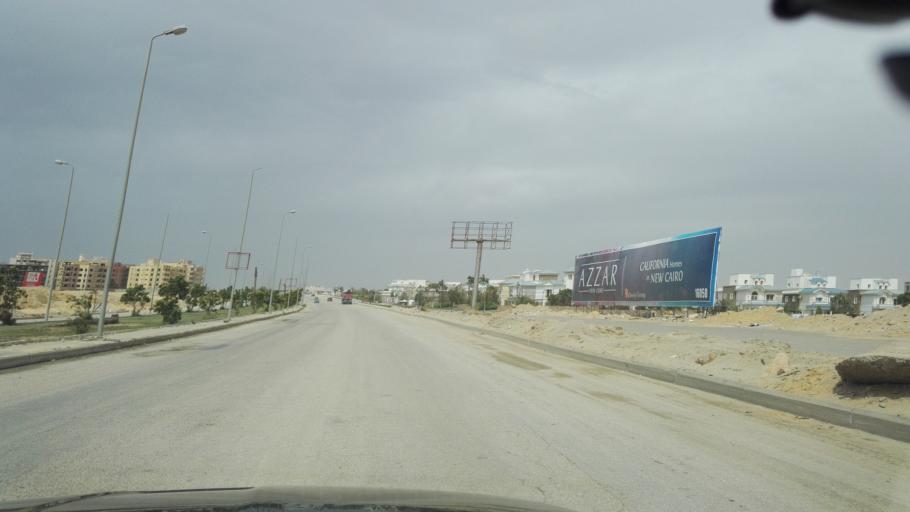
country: EG
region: Muhafazat al Qalyubiyah
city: Al Khankah
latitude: 30.0296
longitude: 31.5291
